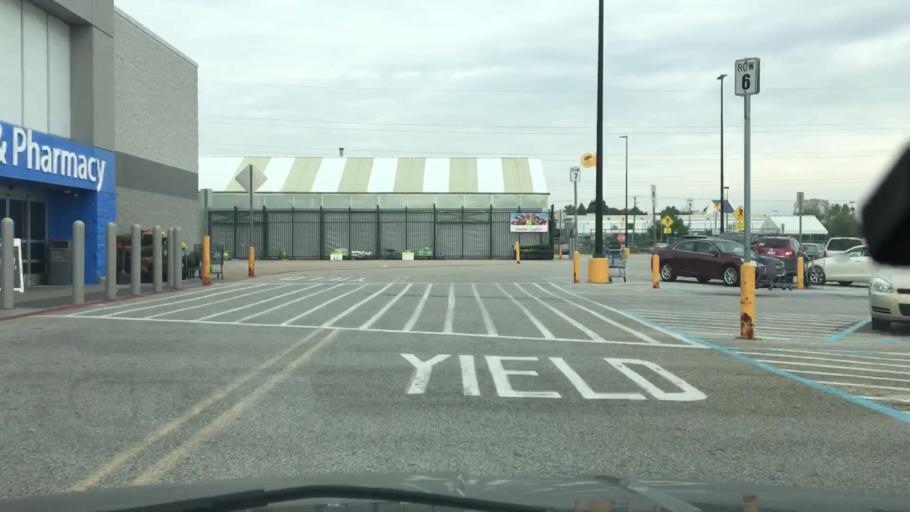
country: US
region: Michigan
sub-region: Berrien County
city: Fair Plain
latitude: 42.0778
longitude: -86.4248
